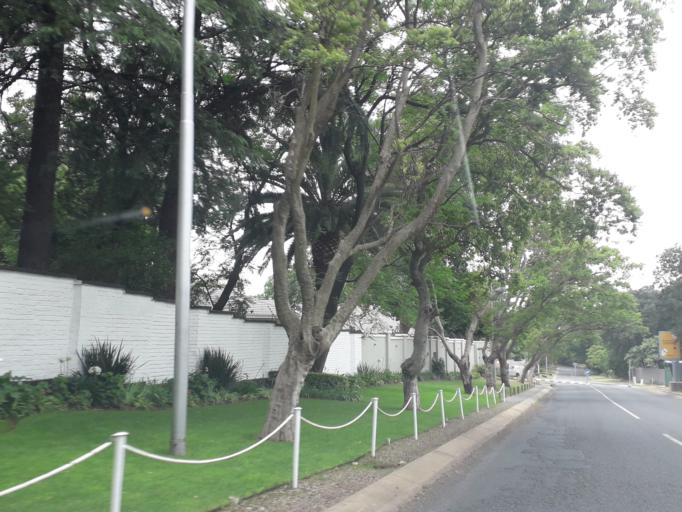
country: ZA
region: Gauteng
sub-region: City of Johannesburg Metropolitan Municipality
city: Midrand
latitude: -26.0456
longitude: 28.0425
